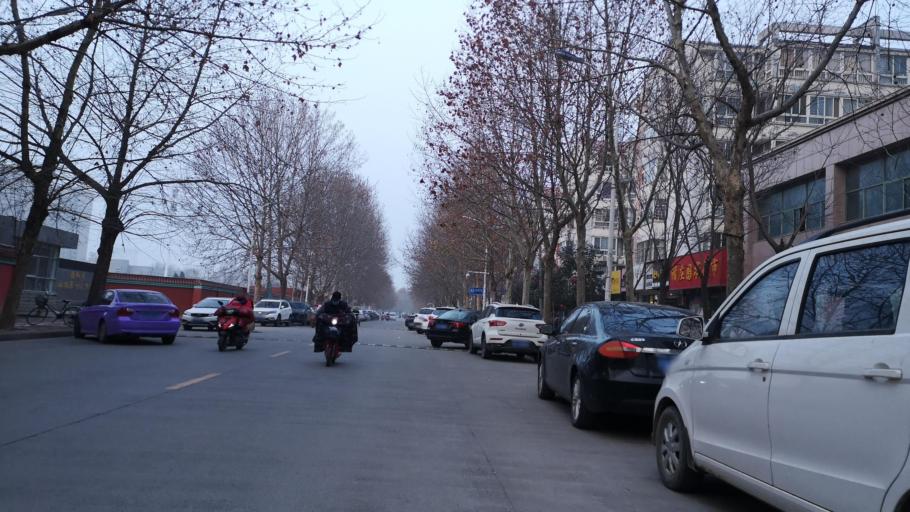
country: CN
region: Henan Sheng
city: Zhongyuanlu
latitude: 35.7543
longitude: 115.0609
